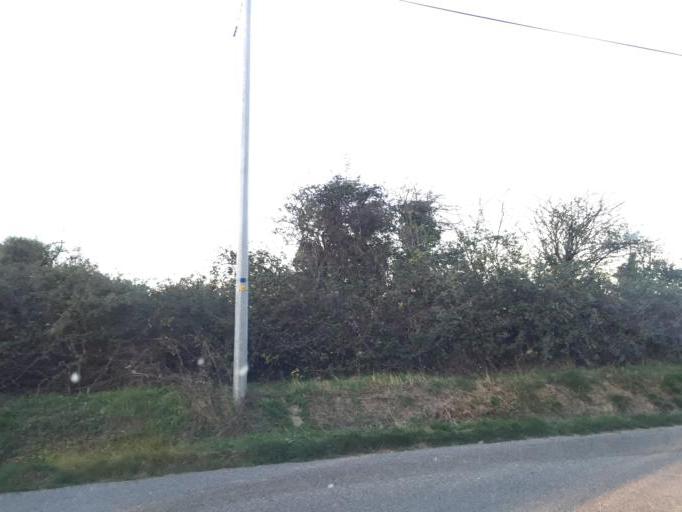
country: FR
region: Provence-Alpes-Cote d'Azur
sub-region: Departement du Vaucluse
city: Camaret-sur-Aigues
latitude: 44.1622
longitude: 4.8949
